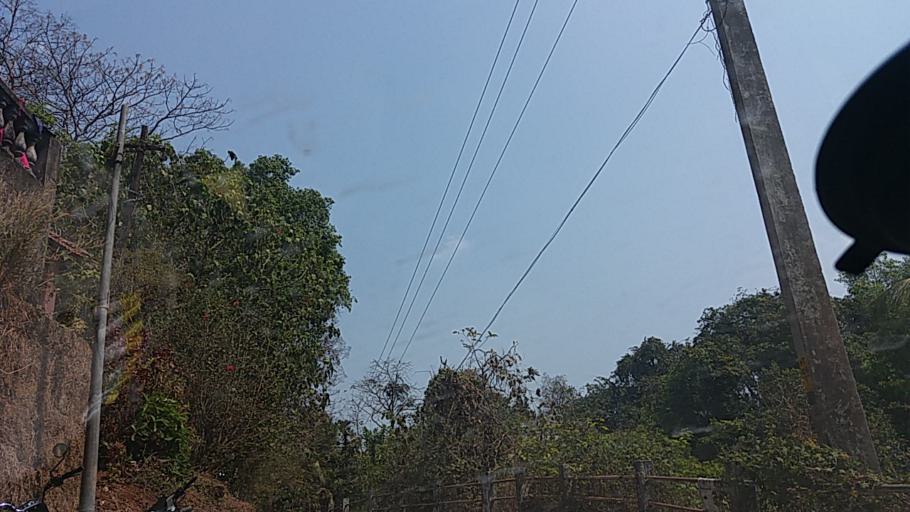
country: IN
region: Goa
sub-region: South Goa
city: Sancoale
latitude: 15.3676
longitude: 73.9158
